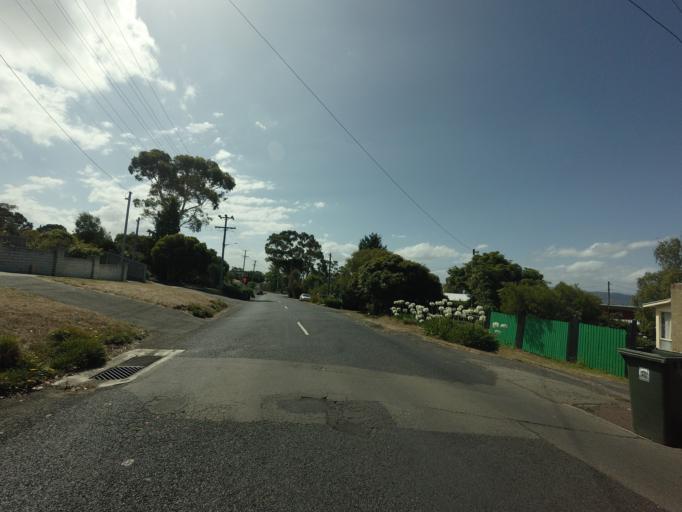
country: AU
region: Tasmania
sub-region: Hobart
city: Dynnyrne
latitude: -42.9153
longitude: 147.3240
